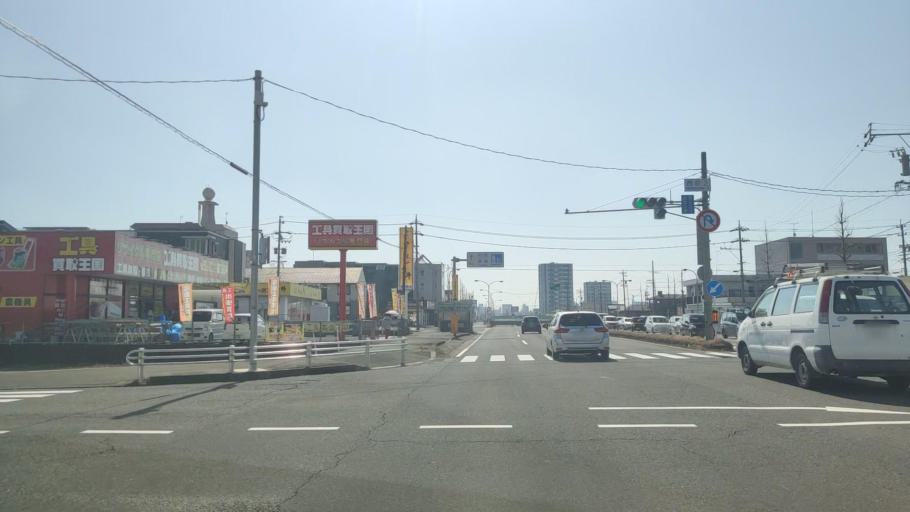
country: JP
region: Gifu
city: Gifu-shi
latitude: 35.4087
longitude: 136.7271
